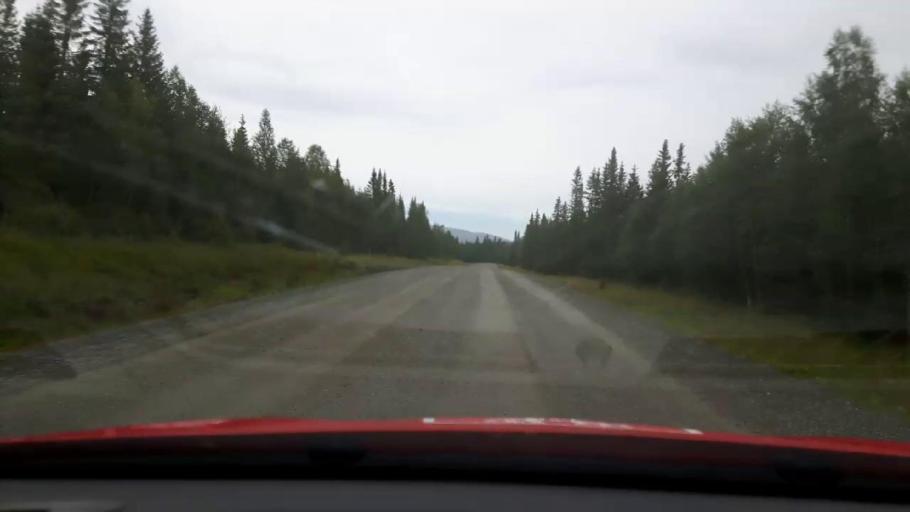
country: SE
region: Jaemtland
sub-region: Are Kommun
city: Are
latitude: 63.4497
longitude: 12.6571
